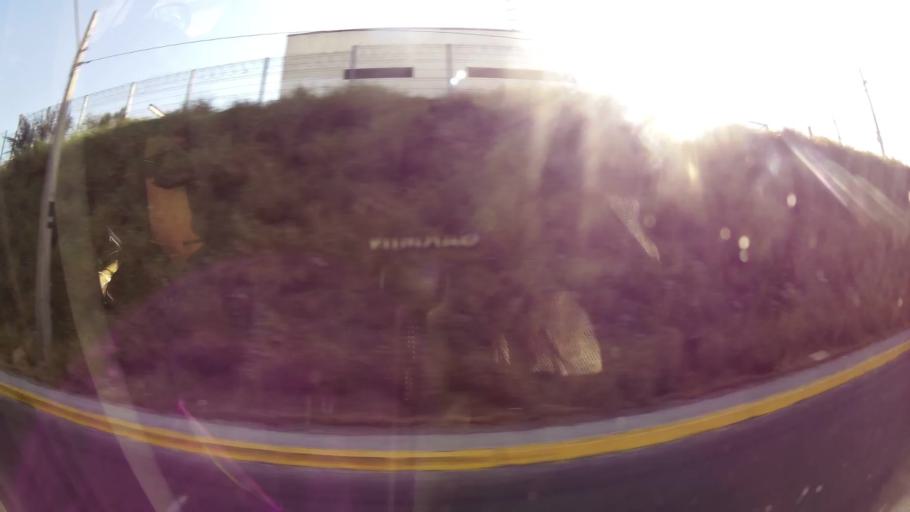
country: CL
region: Santiago Metropolitan
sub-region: Provincia de Maipo
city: San Bernardo
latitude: -33.5285
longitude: -70.6884
